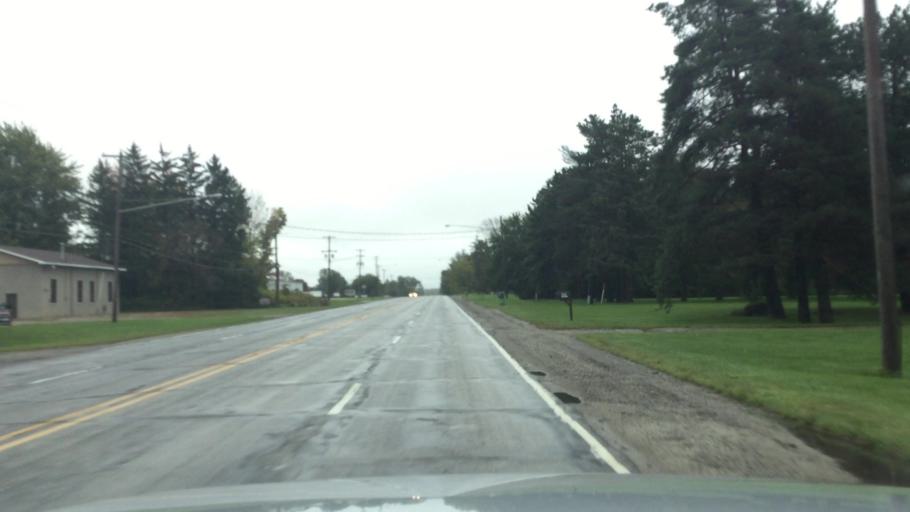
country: US
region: Michigan
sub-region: Saginaw County
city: Bridgeport
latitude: 43.3431
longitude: -83.8498
